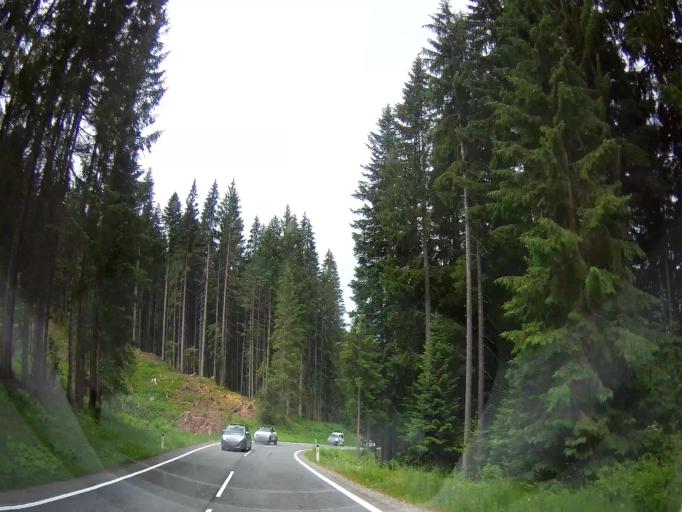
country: AT
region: Salzburg
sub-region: Politischer Bezirk Zell am See
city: Dienten am Hochkonig
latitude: 47.4029
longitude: 12.9883
